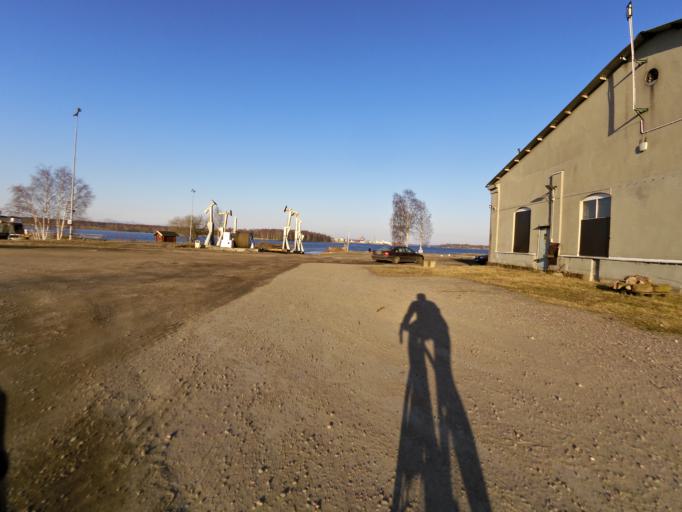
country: SE
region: Gaevleborg
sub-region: Gavle Kommun
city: Gavle
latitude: 60.6790
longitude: 17.1844
